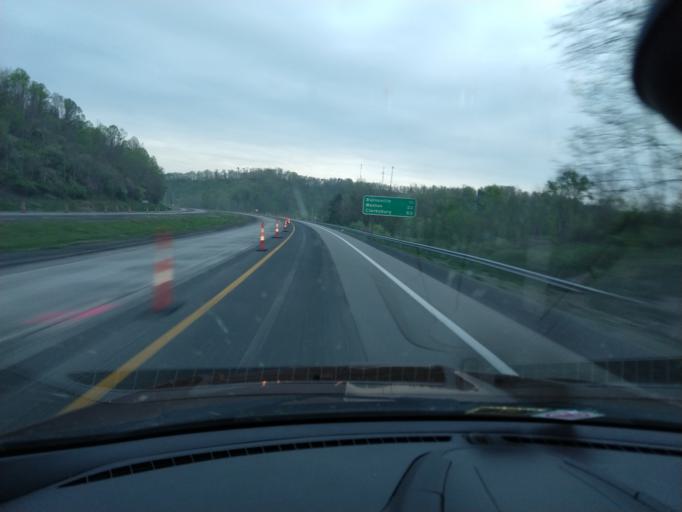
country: US
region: West Virginia
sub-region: Braxton County
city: Sutton
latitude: 38.7180
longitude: -80.6604
